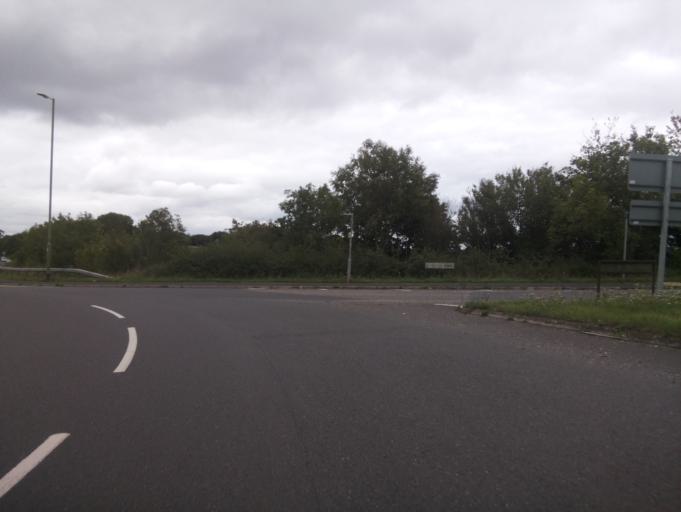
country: GB
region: England
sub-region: Devon
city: Marldon
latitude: 50.4513
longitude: -3.5909
